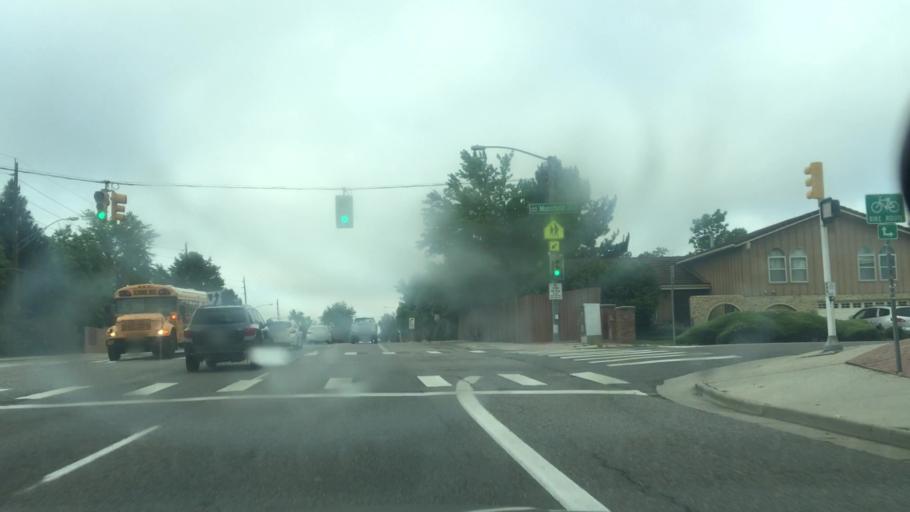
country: US
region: Colorado
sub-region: Arapahoe County
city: Castlewood
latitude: 39.6449
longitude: -104.8852
